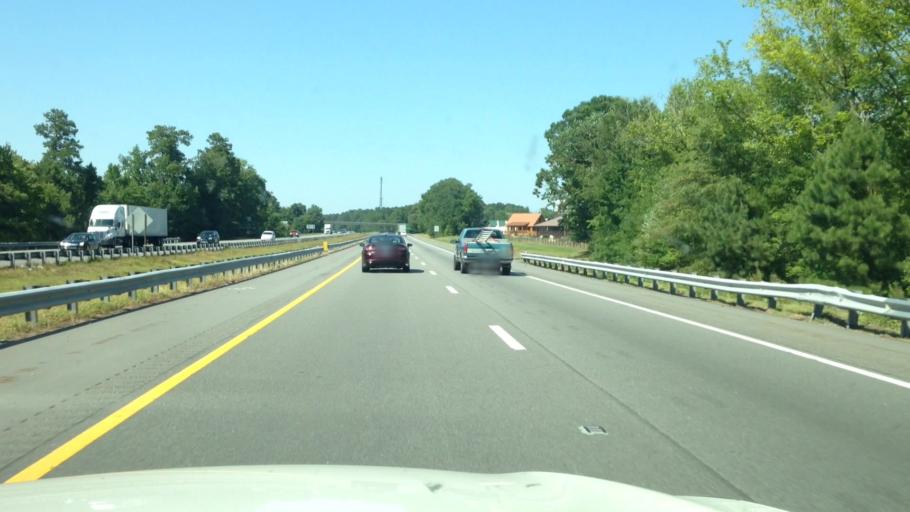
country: US
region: North Carolina
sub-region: Nash County
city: Red Oak
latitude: 36.0702
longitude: -77.8173
